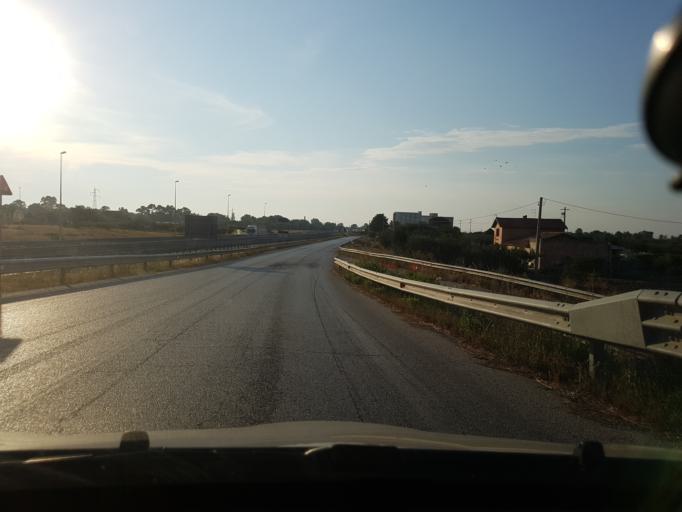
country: IT
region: Apulia
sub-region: Provincia di Foggia
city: Carapelle
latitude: 41.3953
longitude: 15.6597
